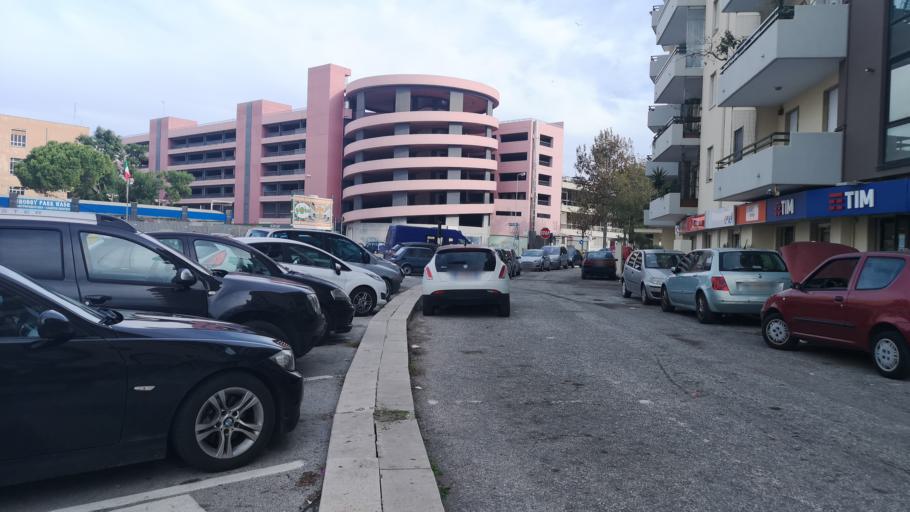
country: IT
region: Apulia
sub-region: Provincia di Bari
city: Bari
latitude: 41.1157
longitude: 16.8848
